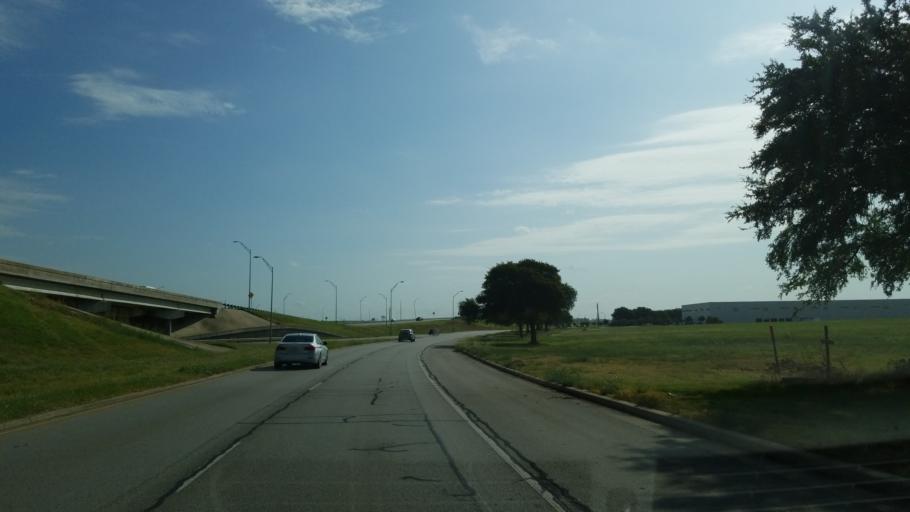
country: US
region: Texas
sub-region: Tarrant County
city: Euless
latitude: 32.8370
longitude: -97.0554
